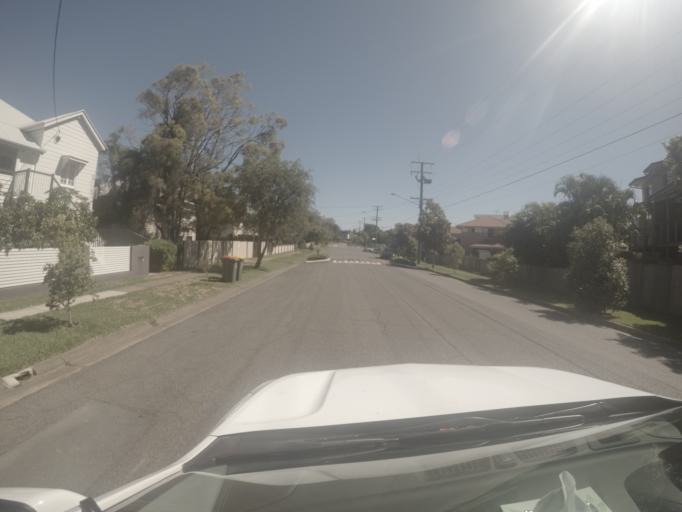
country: AU
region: Queensland
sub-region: Brisbane
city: Rocklea
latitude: -27.5343
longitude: 152.9862
